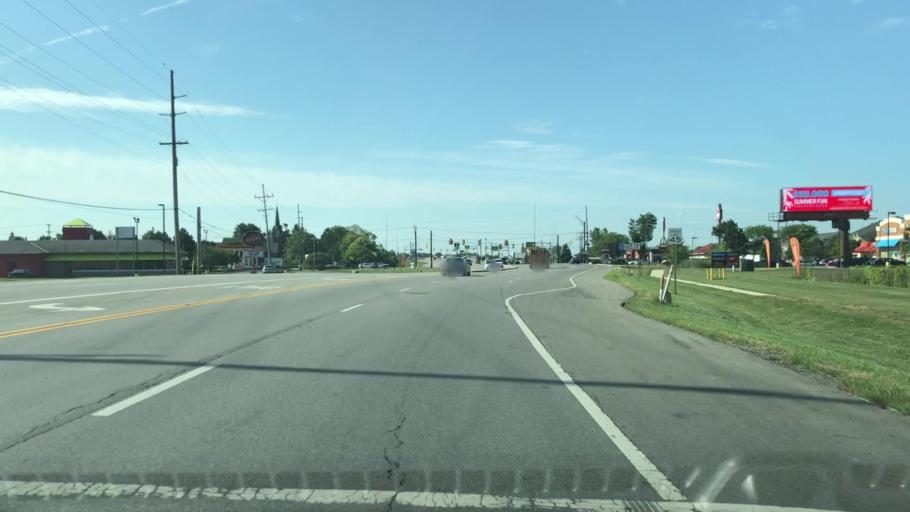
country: US
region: Ohio
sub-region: Franklin County
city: Lincoln Village
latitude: 39.9834
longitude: -83.1507
